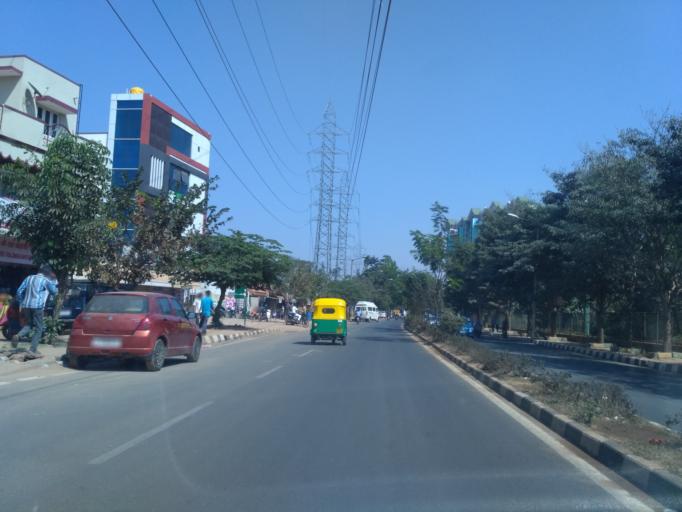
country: IN
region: Karnataka
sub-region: Bangalore Urban
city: Yelahanka
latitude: 13.0980
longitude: 77.5684
